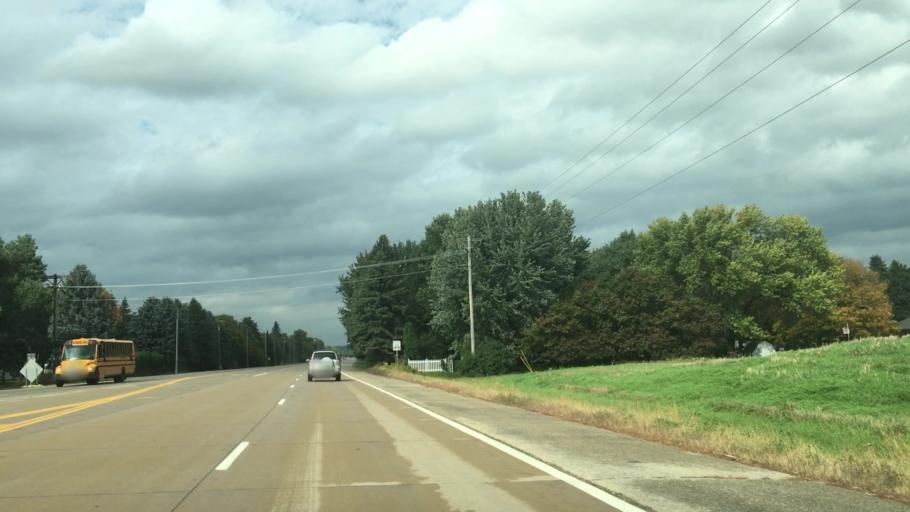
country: US
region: Minnesota
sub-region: Olmsted County
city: Rochester
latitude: 43.9775
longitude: -92.4397
